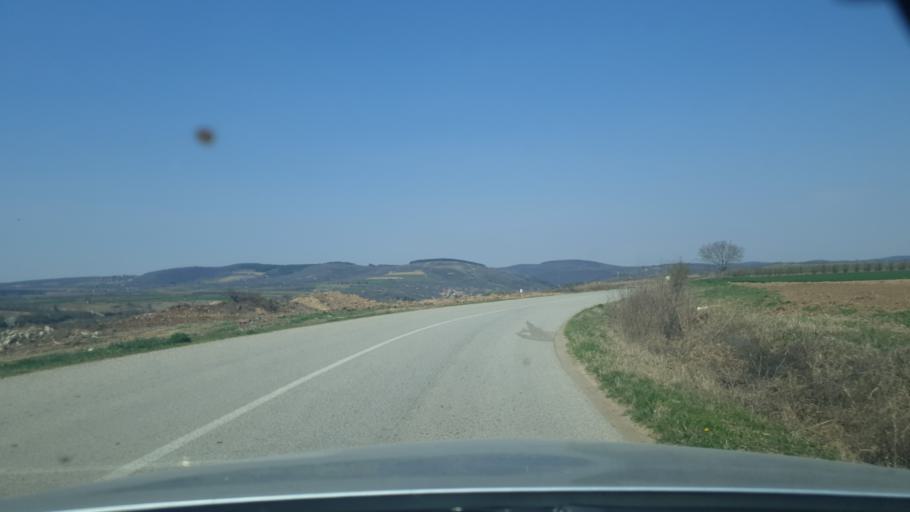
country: RS
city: Vrdnik
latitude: 45.0846
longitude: 19.7689
